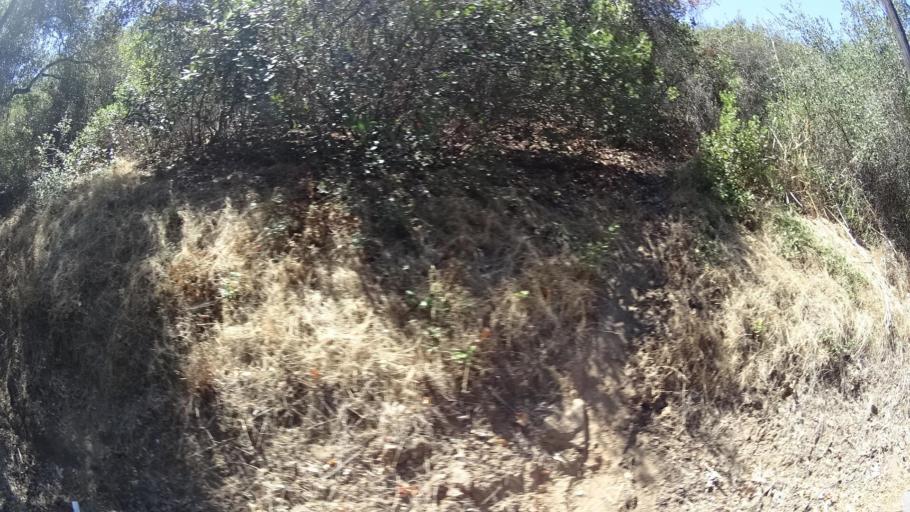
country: US
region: California
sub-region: San Diego County
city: Rainbow
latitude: 33.3260
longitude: -117.1078
